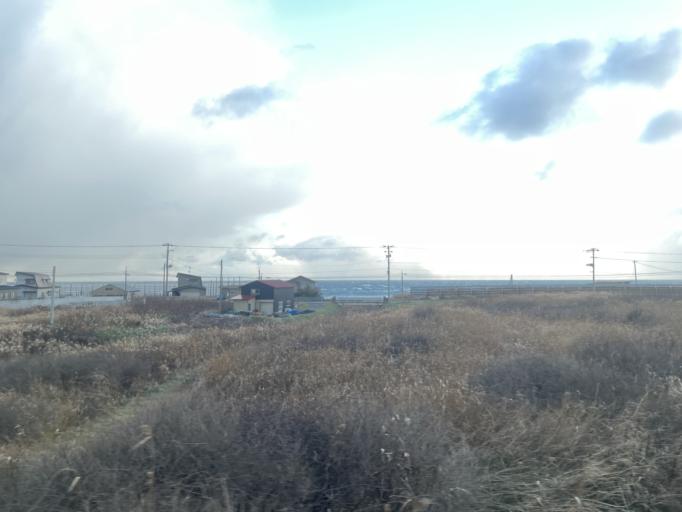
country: JP
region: Aomori
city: Mutsu
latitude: 41.0934
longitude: 141.2500
